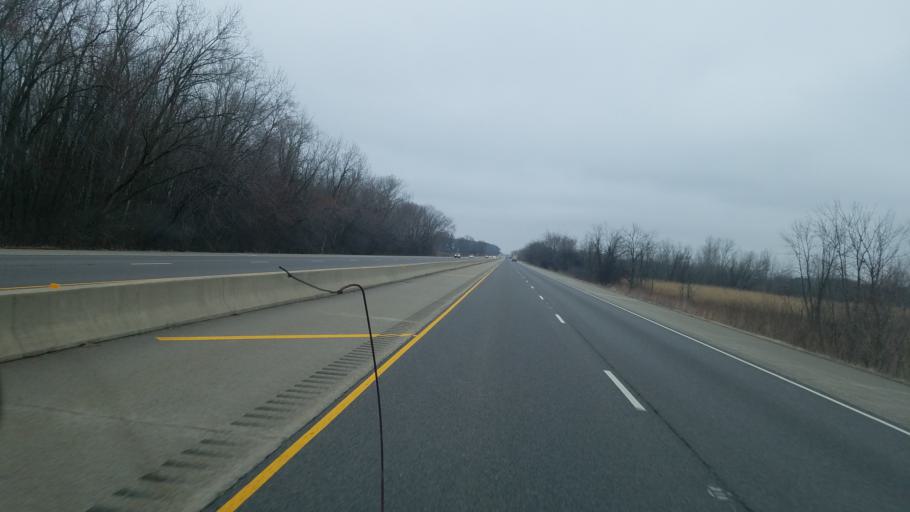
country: US
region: Illinois
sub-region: Lake County
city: Wadsworth
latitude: 42.4122
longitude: -87.9379
